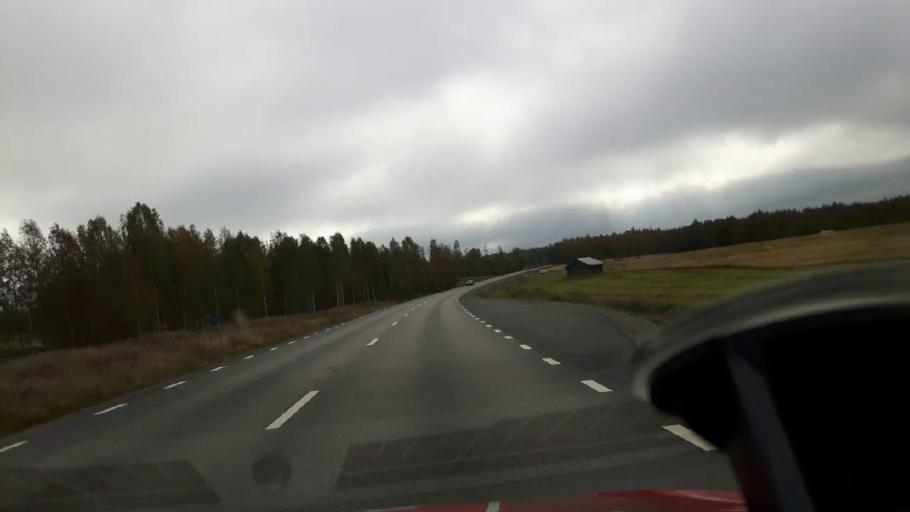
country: SE
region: Gaevleborg
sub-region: Ljusdals Kommun
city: Farila
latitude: 61.8639
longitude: 15.7375
